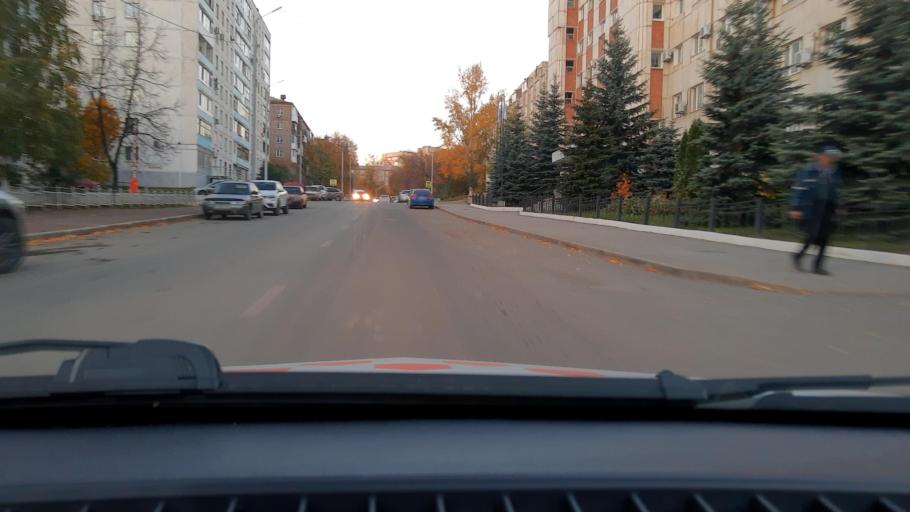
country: RU
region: Bashkortostan
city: Ufa
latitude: 54.7283
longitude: 55.9828
